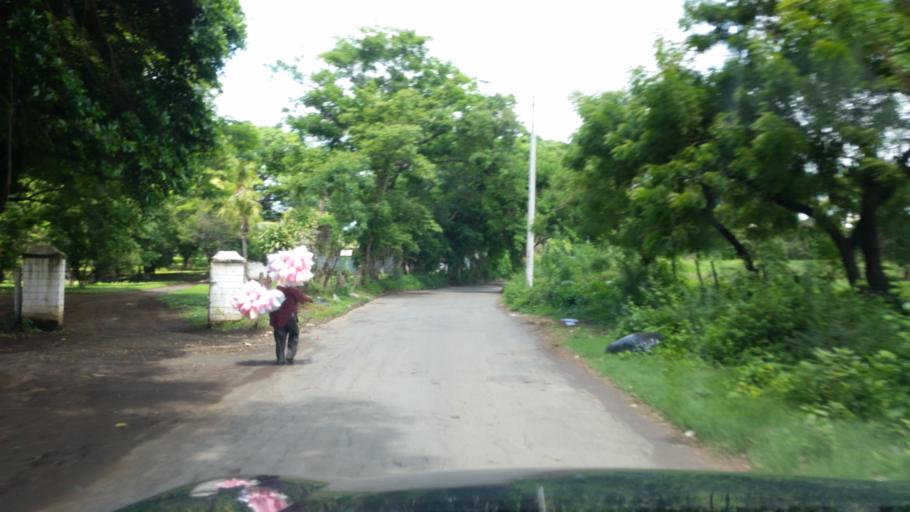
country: NI
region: Managua
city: Managua
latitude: 12.0899
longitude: -86.2224
